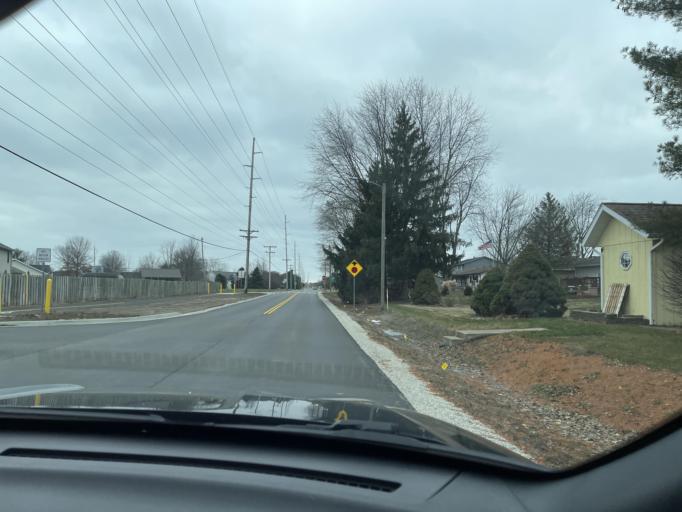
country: US
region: Illinois
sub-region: Sangamon County
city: Rochester
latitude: 39.7633
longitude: -89.5787
